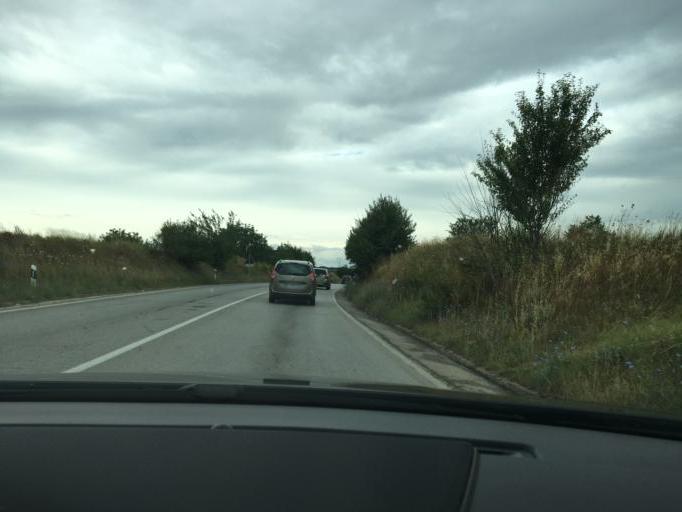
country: MK
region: Staro Nagoricane
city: Staro Nagorichane
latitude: 42.1735
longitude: 21.7923
